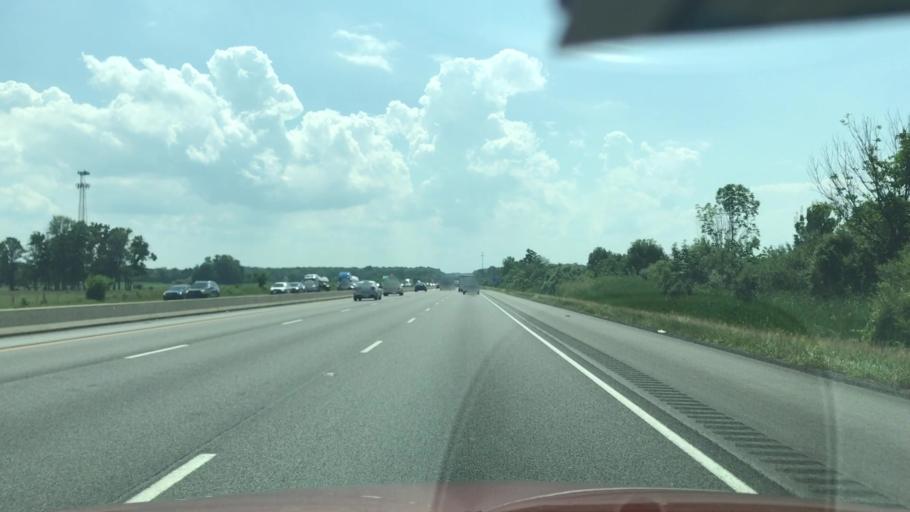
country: US
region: Michigan
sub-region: Berrien County
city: New Buffalo
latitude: 41.7449
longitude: -86.7754
